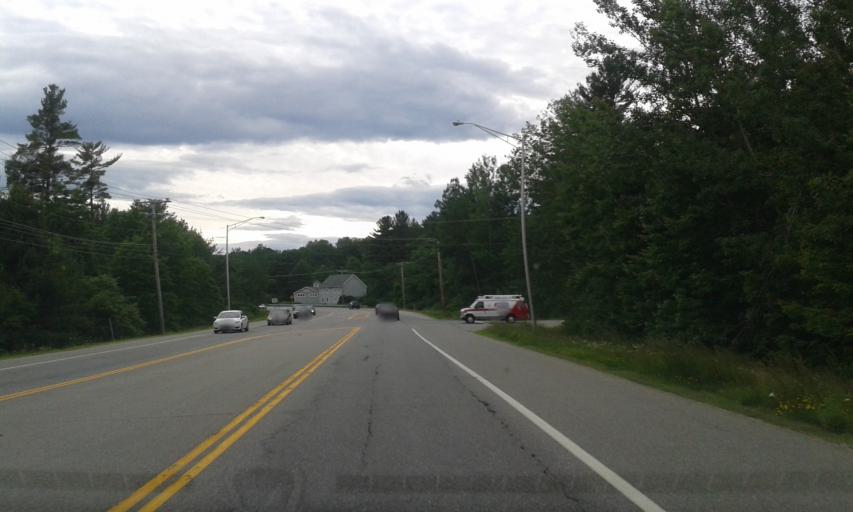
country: US
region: New Hampshire
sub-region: Hillsborough County
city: Litchfield
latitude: 42.8071
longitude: -71.5411
